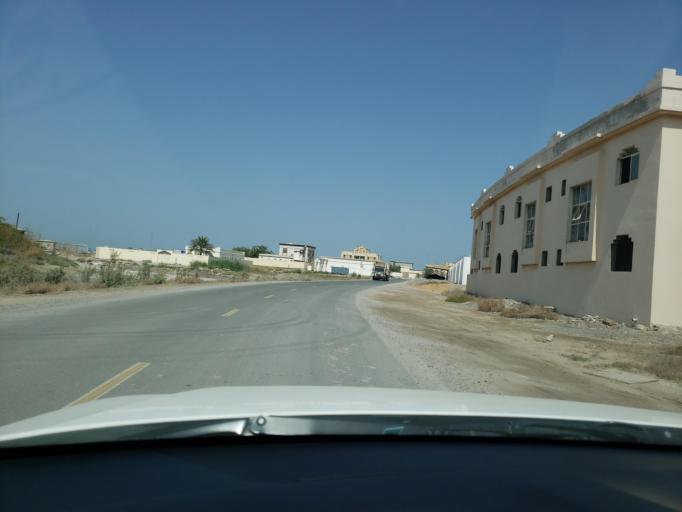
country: AE
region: Ra's al Khaymah
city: Ras al-Khaimah
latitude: 25.8567
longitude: 56.0173
